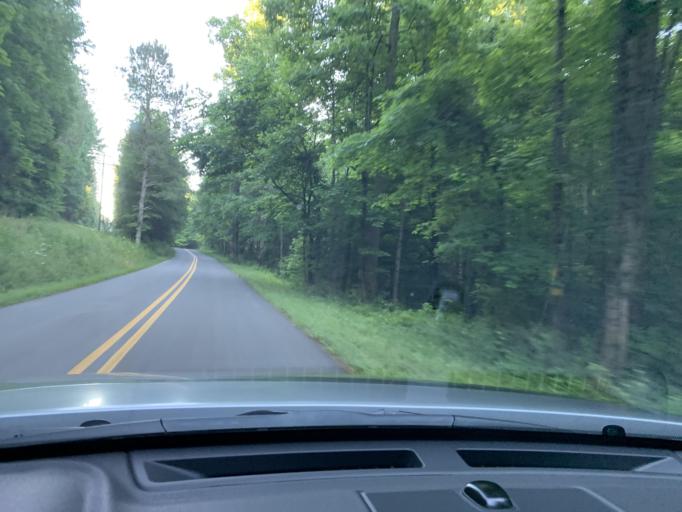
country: US
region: Georgia
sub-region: Bartow County
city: Rydal
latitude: 34.2378
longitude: -84.6669
